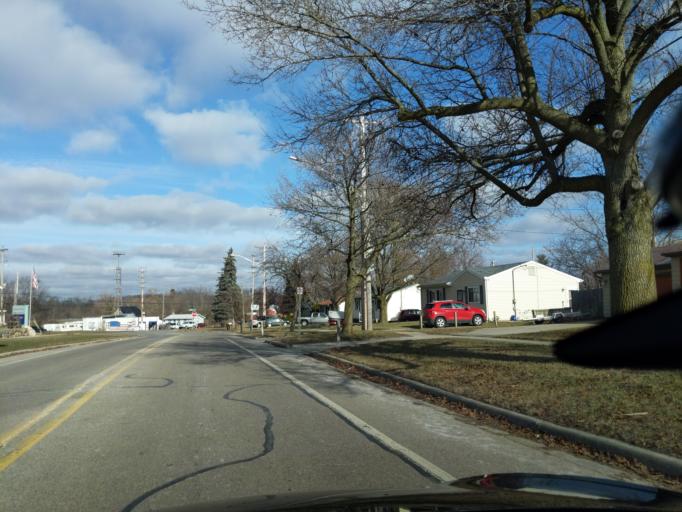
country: US
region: Michigan
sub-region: Ingham County
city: Lansing
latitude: 42.6764
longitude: -84.5726
